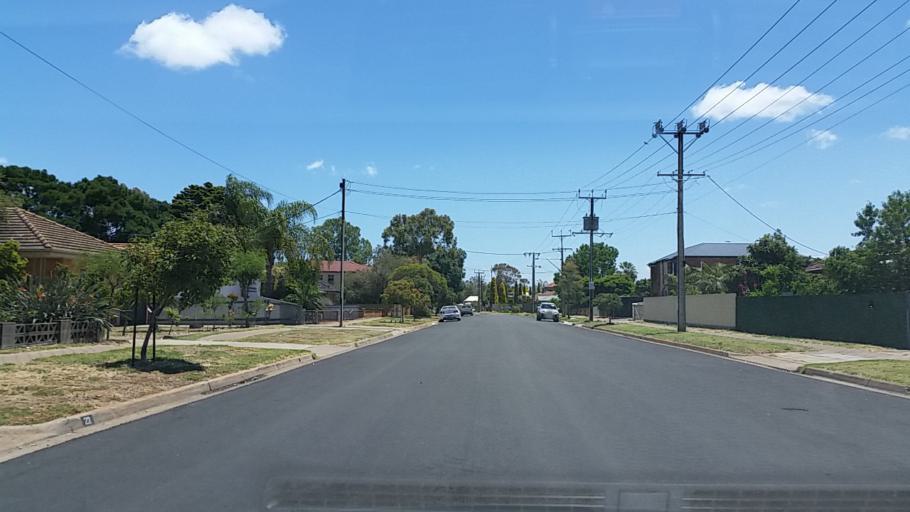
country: AU
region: South Australia
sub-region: Salisbury
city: Salisbury
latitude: -34.7666
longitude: 138.6416
